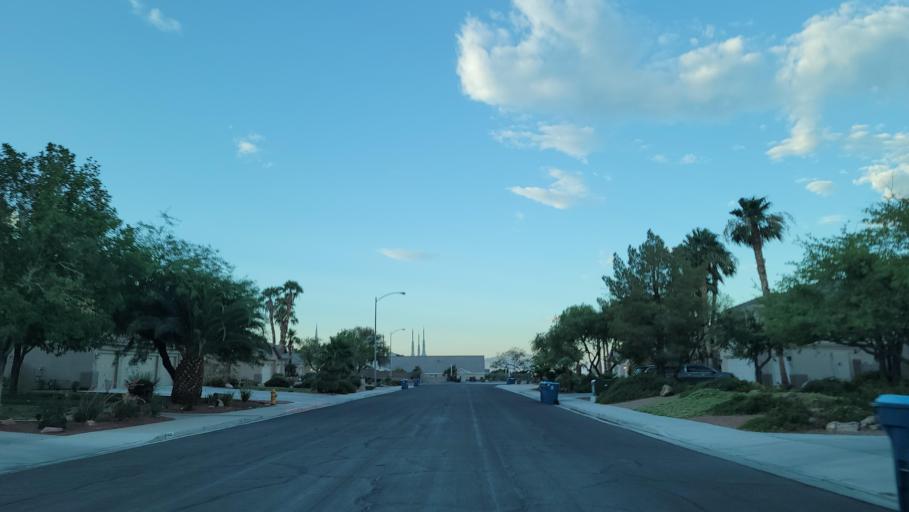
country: US
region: Nevada
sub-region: Clark County
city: Sunrise Manor
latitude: 36.1788
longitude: -115.0205
